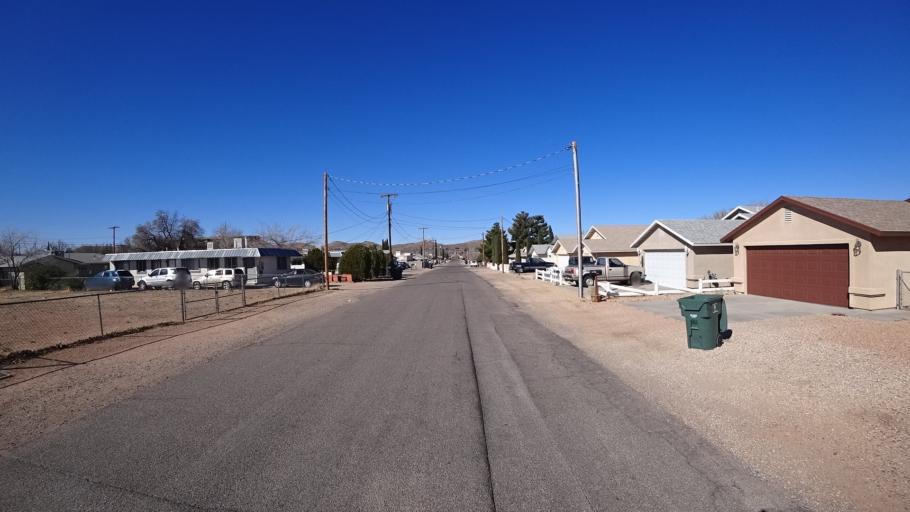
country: US
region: Arizona
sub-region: Mohave County
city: Kingman
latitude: 35.2053
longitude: -114.0277
